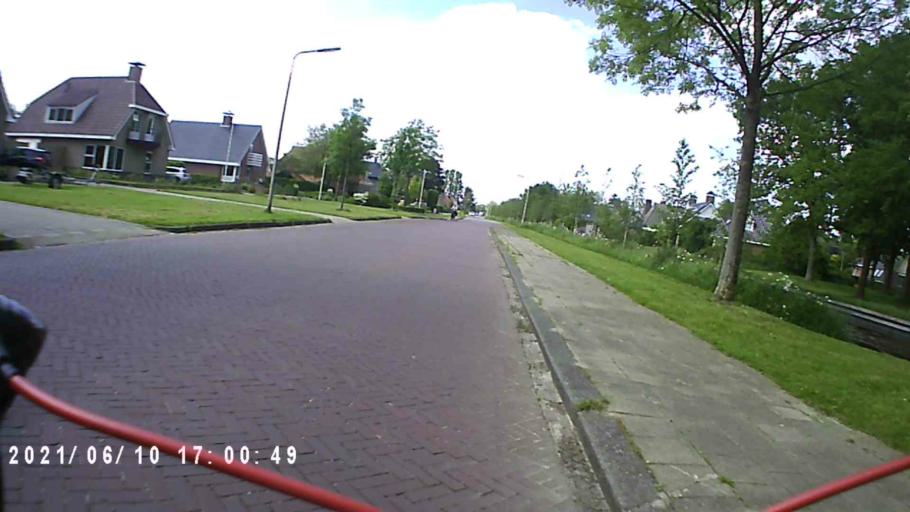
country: NL
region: Friesland
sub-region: Gemeente Kollumerland en Nieuwkruisland
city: Kollum
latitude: 53.2730
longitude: 6.1562
